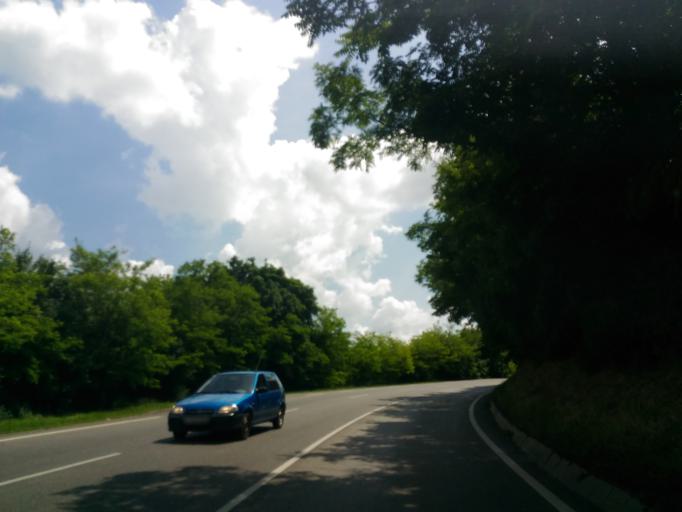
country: HU
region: Baranya
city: Pecs
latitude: 46.1225
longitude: 18.2613
